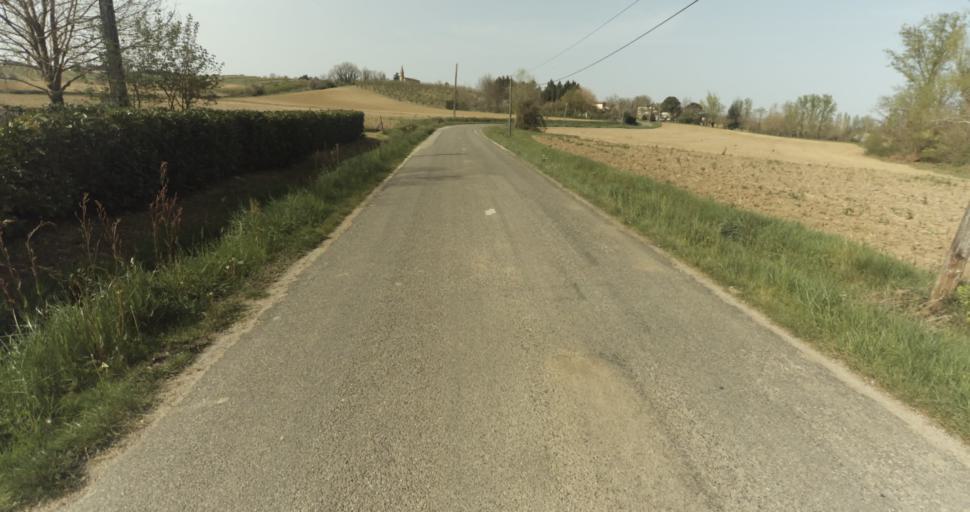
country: FR
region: Midi-Pyrenees
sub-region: Departement du Tarn-et-Garonne
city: Lafrancaise
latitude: 44.1388
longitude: 1.1751
